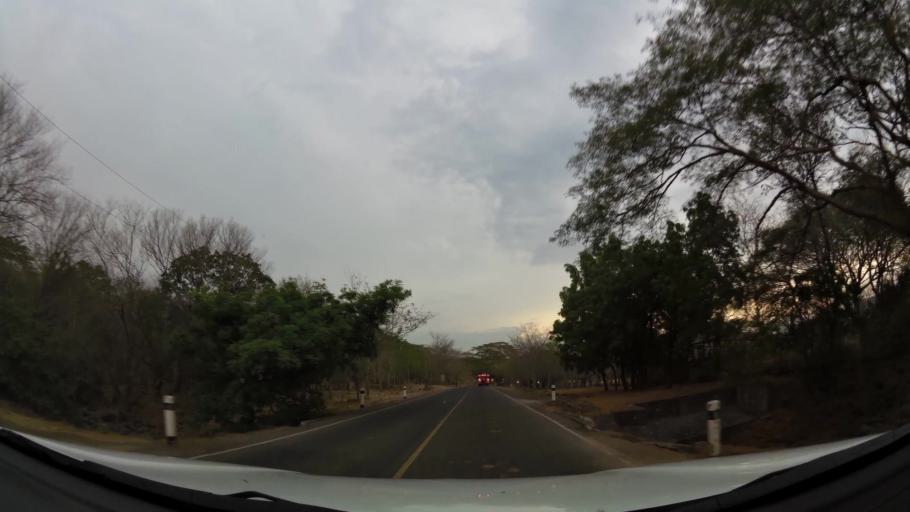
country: NI
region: Leon
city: La Jicaral
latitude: 12.7151
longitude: -86.3949
